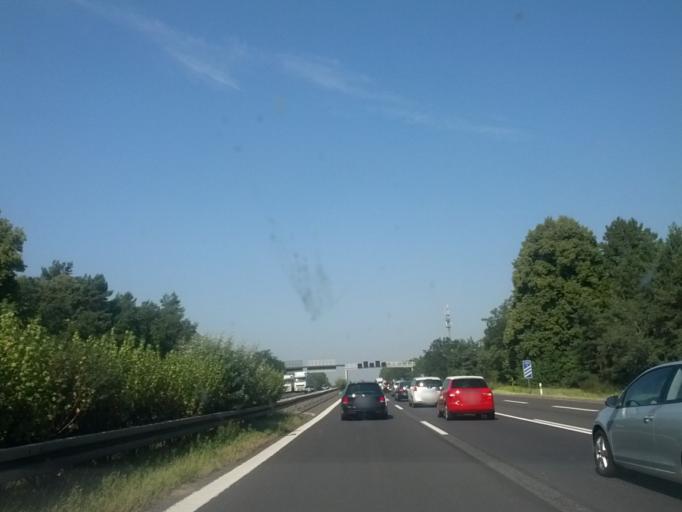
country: DE
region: Brandenburg
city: Michendorf
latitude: 52.2991
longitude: 13.0291
